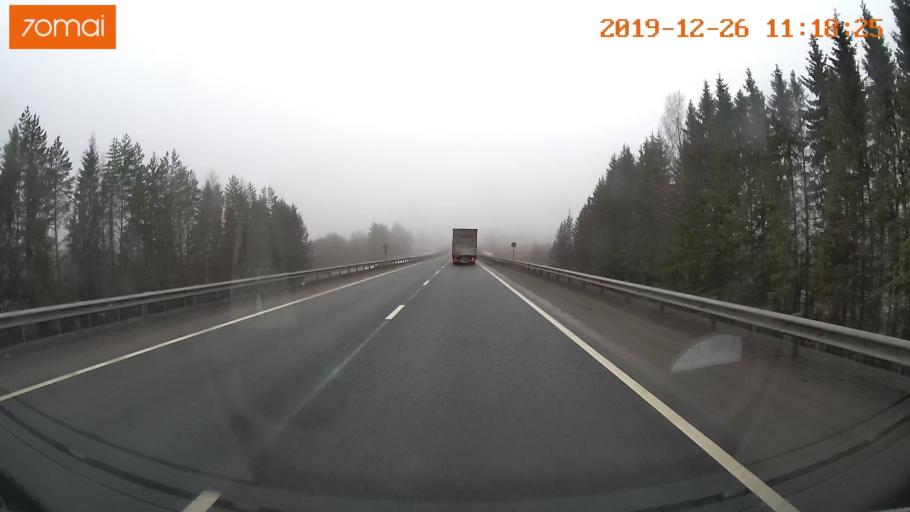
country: RU
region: Vologda
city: Chebsara
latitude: 59.1192
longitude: 39.0346
